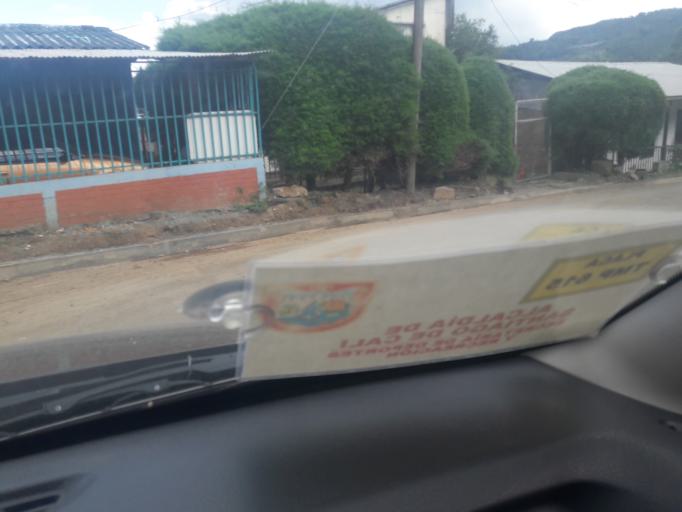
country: CO
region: Valle del Cauca
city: Cali
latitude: 3.4672
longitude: -76.6311
